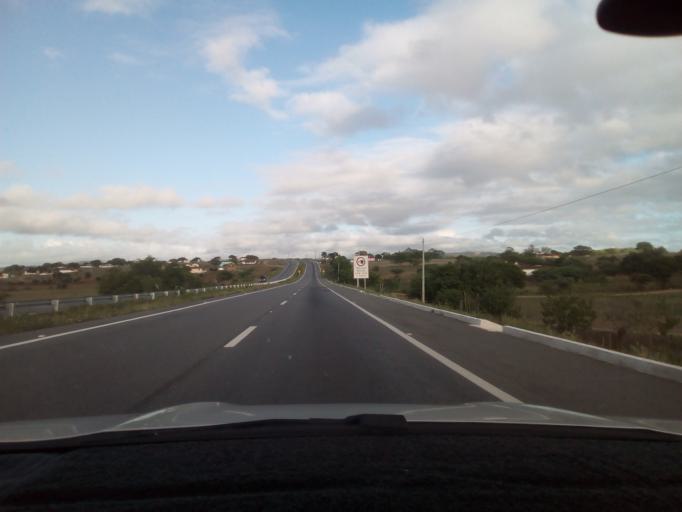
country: BR
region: Paraiba
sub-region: Serra Redonda
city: Alagoa Grande
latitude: -7.2027
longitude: -35.5498
